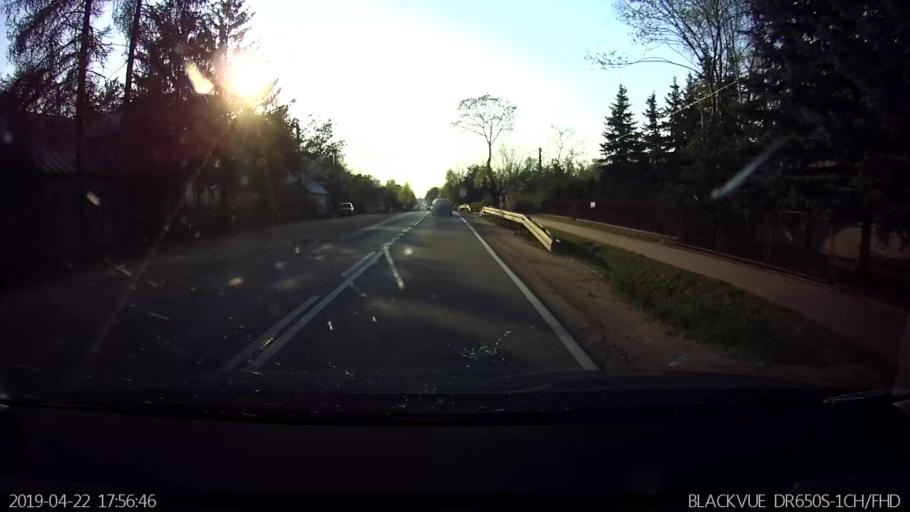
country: PL
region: Masovian Voivodeship
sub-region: Powiat wegrowski
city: Korytnica
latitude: 52.4663
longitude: 21.9023
